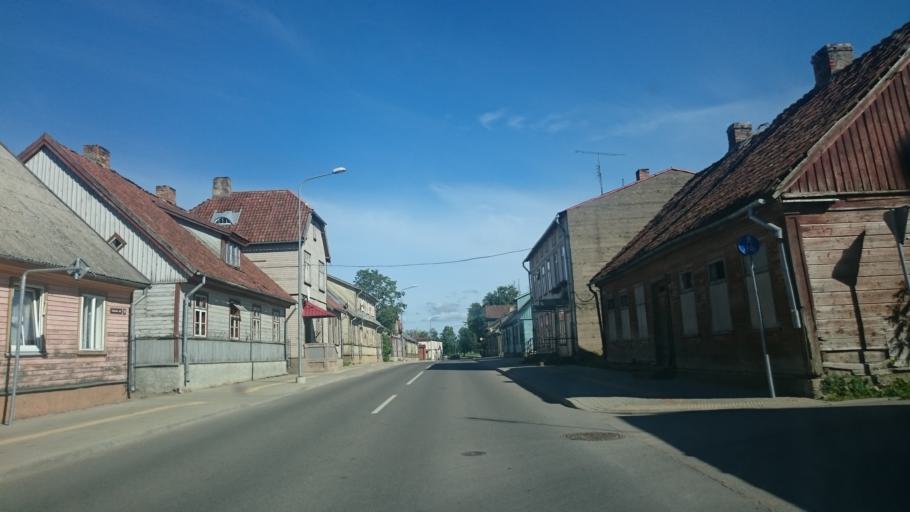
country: LV
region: Aizpute
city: Aizpute
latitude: 56.7170
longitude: 21.6106
